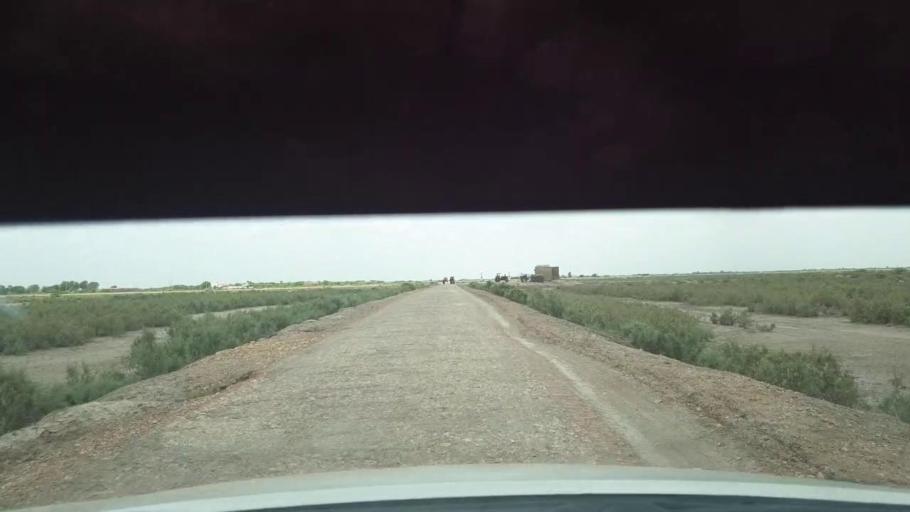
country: PK
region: Sindh
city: Kadhan
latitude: 24.5471
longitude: 69.1248
